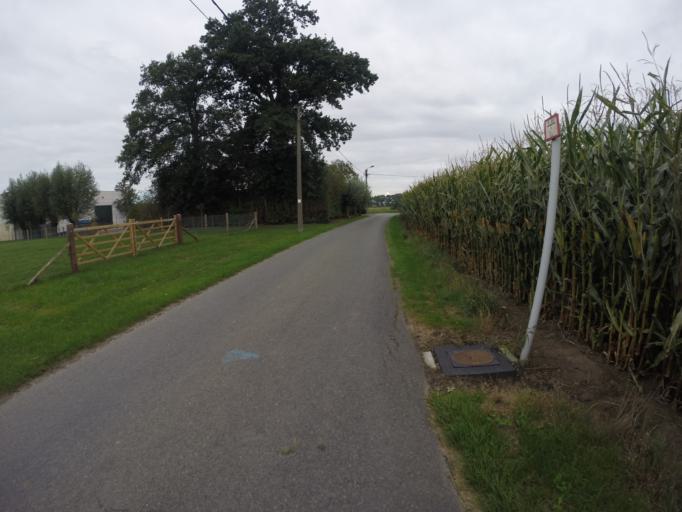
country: BE
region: Flanders
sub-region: Provincie West-Vlaanderen
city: Ruiselede
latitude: 51.0494
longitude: 3.3617
